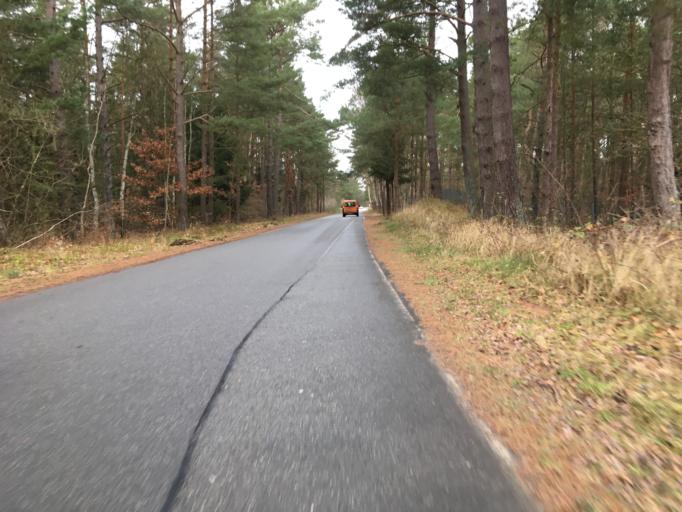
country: DE
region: Mecklenburg-Vorpommern
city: Ostseebad Binz
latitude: 54.4529
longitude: 13.5642
